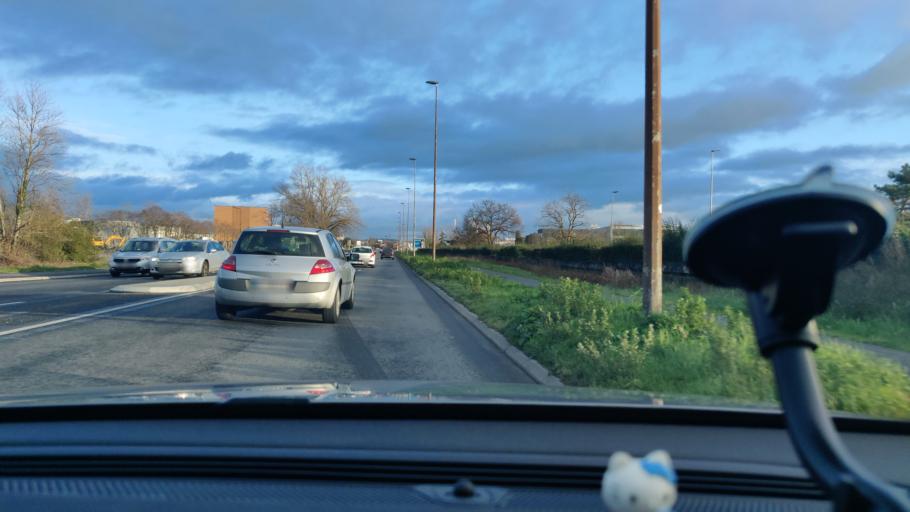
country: FR
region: Midi-Pyrenees
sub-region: Departement de la Haute-Garonne
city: Cugnaux
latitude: 43.5662
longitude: 1.3800
